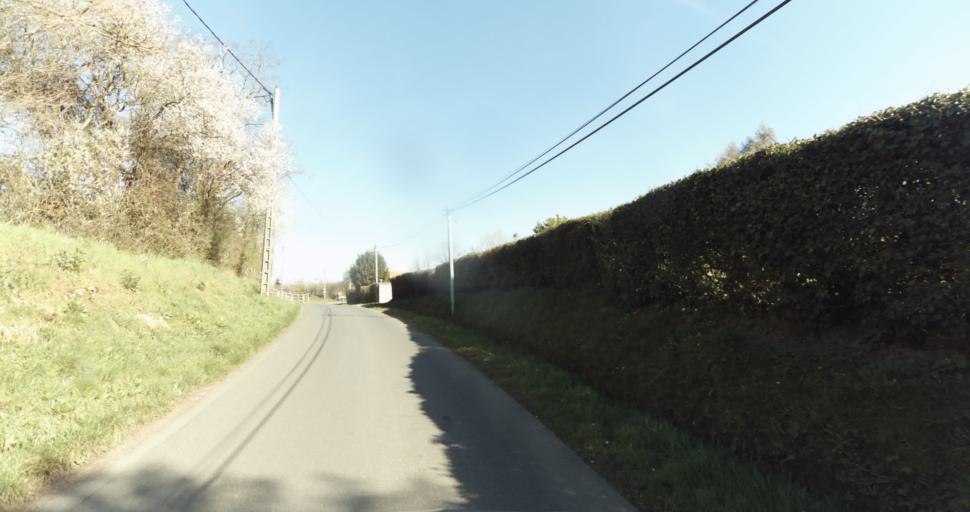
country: FR
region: Lower Normandy
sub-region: Departement du Calvados
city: Saint-Pierre-sur-Dives
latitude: 49.0374
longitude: 0.0459
